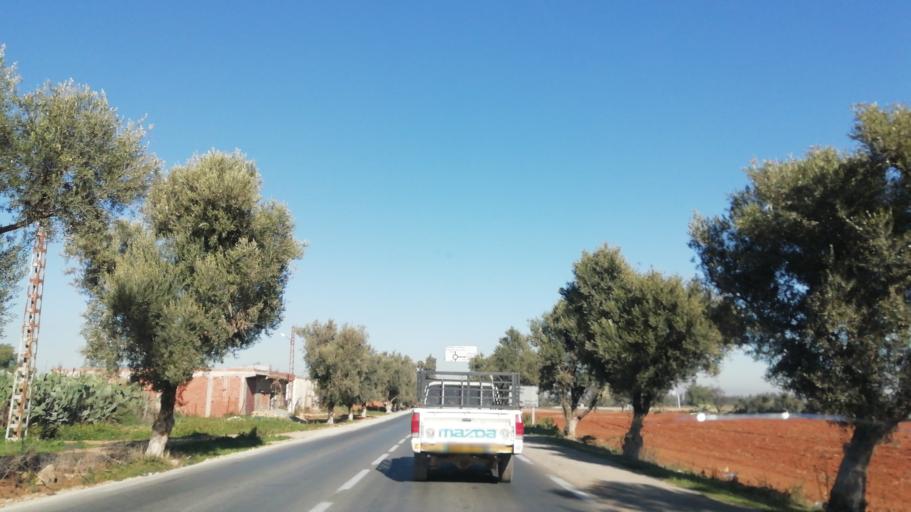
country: DZ
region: Mascara
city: Mascara
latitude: 35.2726
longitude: 0.1286
